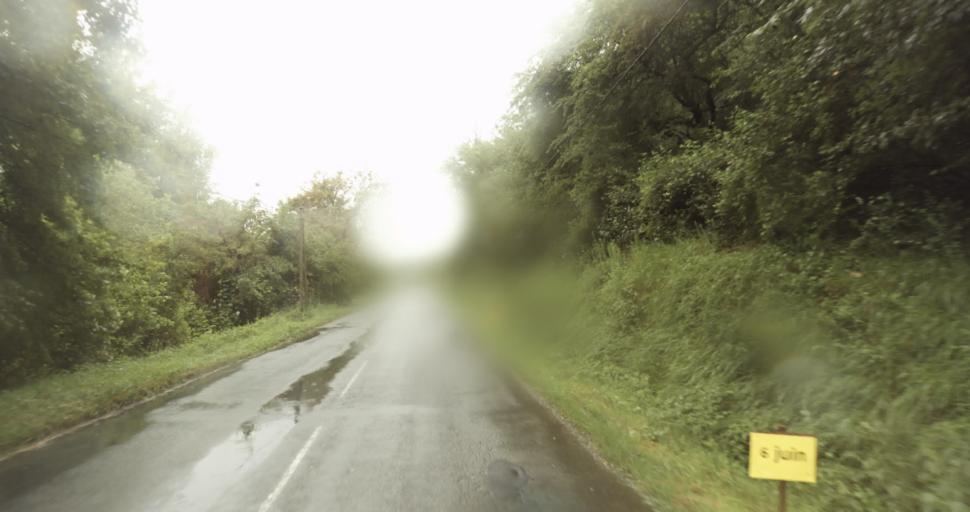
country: FR
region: Aquitaine
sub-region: Departement de la Dordogne
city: Le Bugue
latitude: 44.8363
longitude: 0.9000
